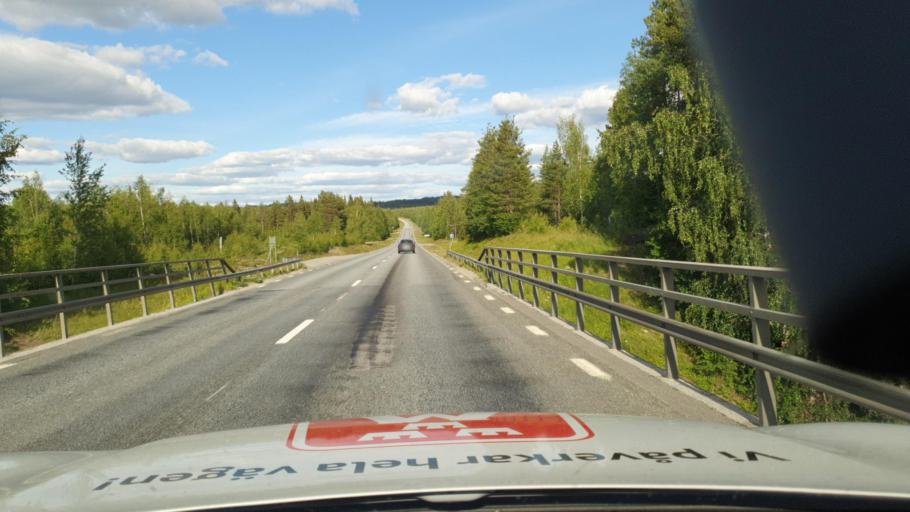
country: SE
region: Vaesterbotten
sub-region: Lycksele Kommun
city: Lycksele
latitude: 64.5111
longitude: 18.3435
